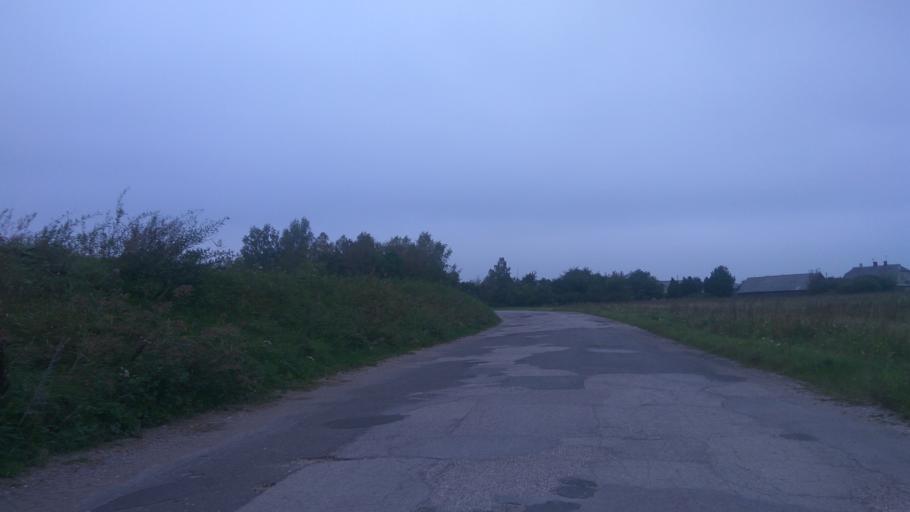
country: LV
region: Rucavas
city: Rucava
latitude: 56.1544
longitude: 21.1707
